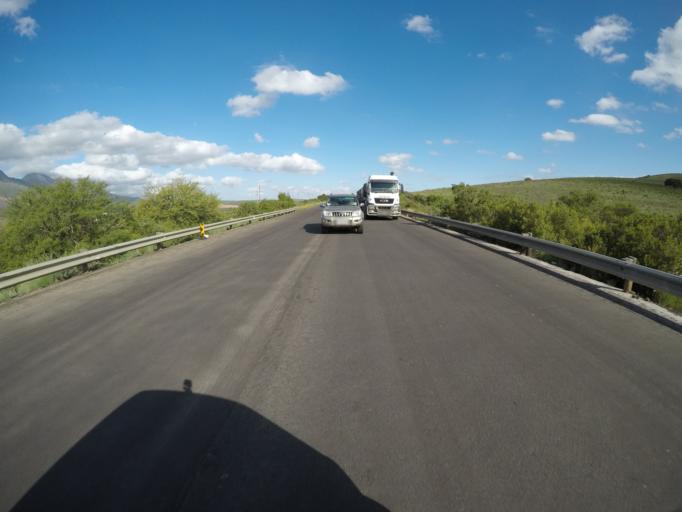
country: ZA
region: Western Cape
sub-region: Cape Winelands District Municipality
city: Ashton
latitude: -33.9324
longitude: 20.2099
